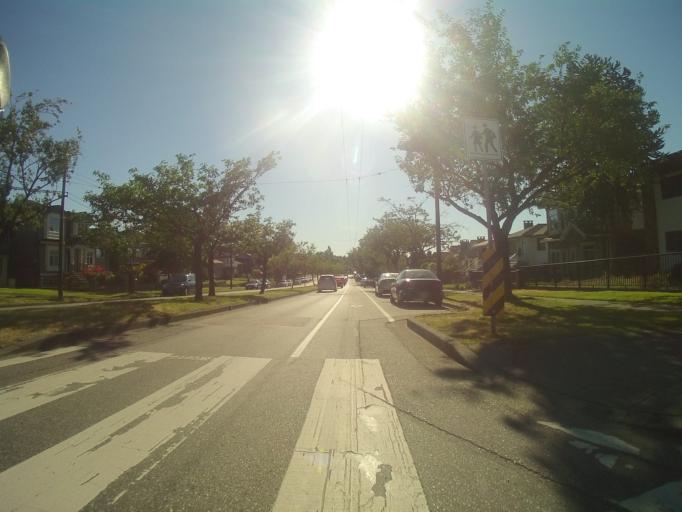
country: CA
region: British Columbia
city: Vancouver
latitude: 49.2507
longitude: -123.0524
